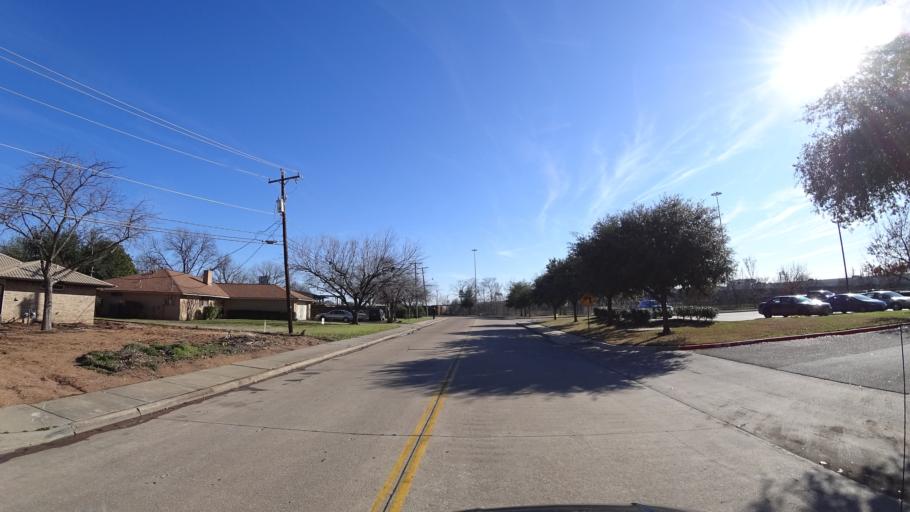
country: US
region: Texas
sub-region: Denton County
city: Highland Village
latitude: 33.0738
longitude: -97.0186
